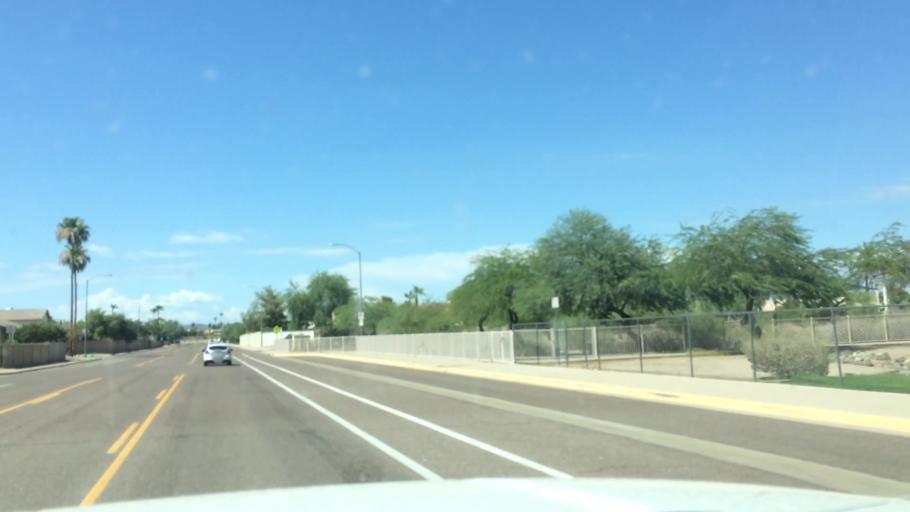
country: US
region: Arizona
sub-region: Maricopa County
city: Sun City
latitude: 33.6483
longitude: -112.2463
